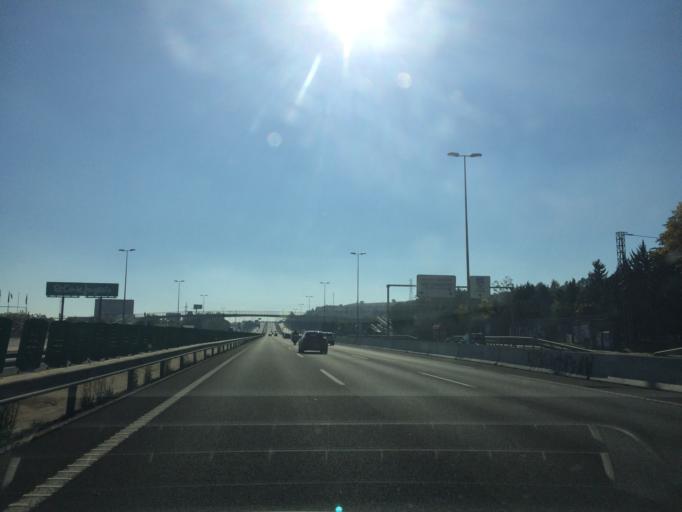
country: ES
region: Madrid
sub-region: Provincia de Madrid
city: San Sebastian de los Reyes
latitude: 40.5905
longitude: -3.5829
